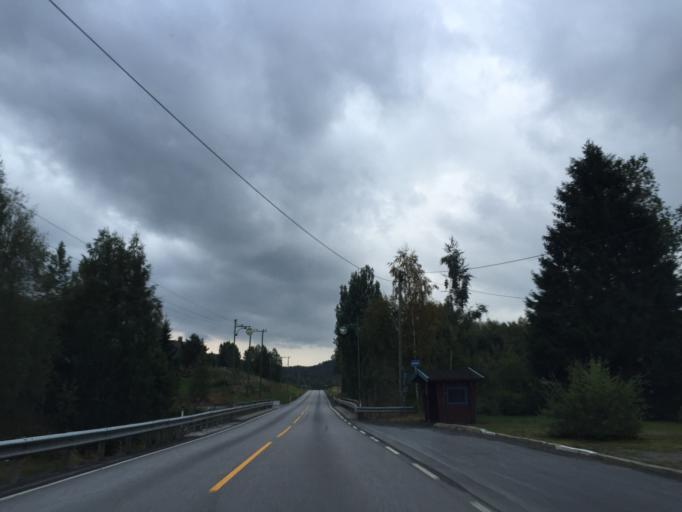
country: NO
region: Hedmark
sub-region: Nord-Odal
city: Sand
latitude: 60.4405
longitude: 11.5012
